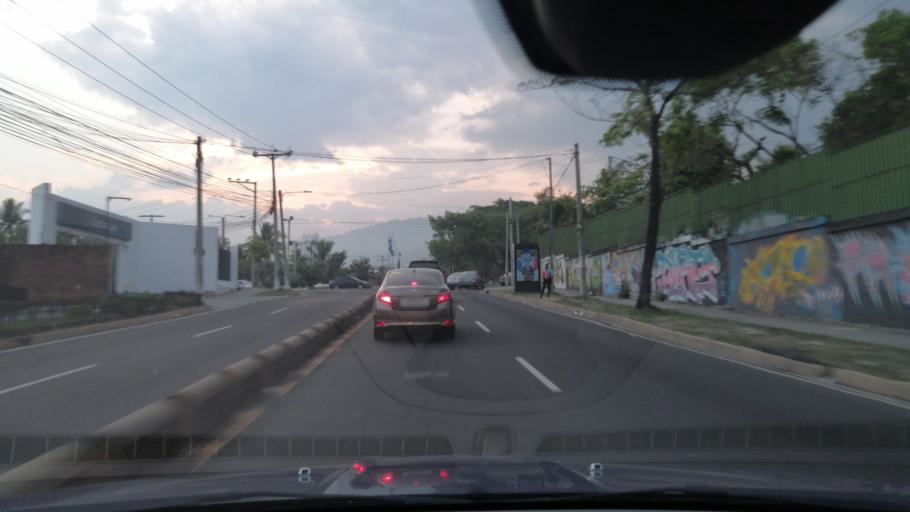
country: SV
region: San Salvador
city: San Salvador
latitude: 13.7057
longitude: -89.2072
